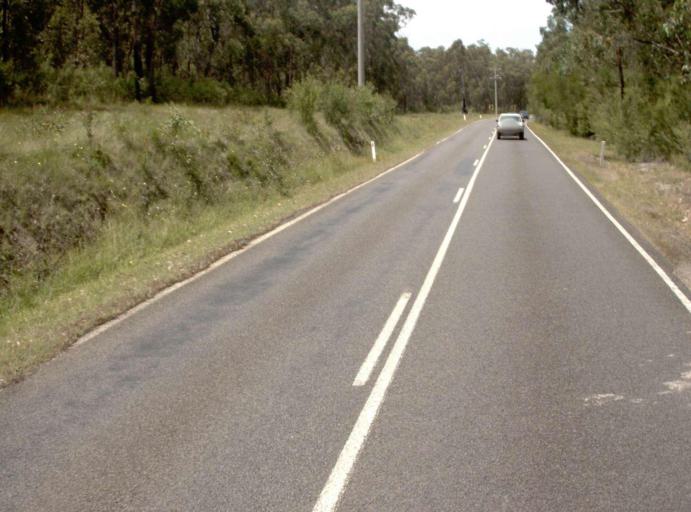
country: AU
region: Victoria
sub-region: Latrobe
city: Moe
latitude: -38.0616
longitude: 146.3351
